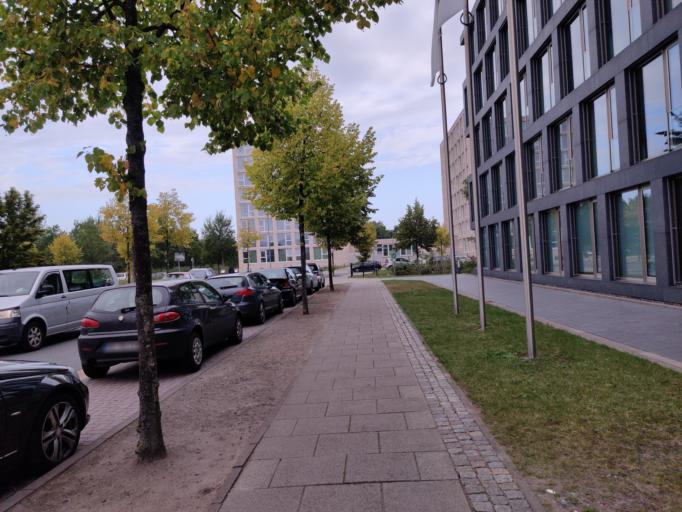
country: DE
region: Bremen
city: Bremen
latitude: 53.1042
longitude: 8.8596
